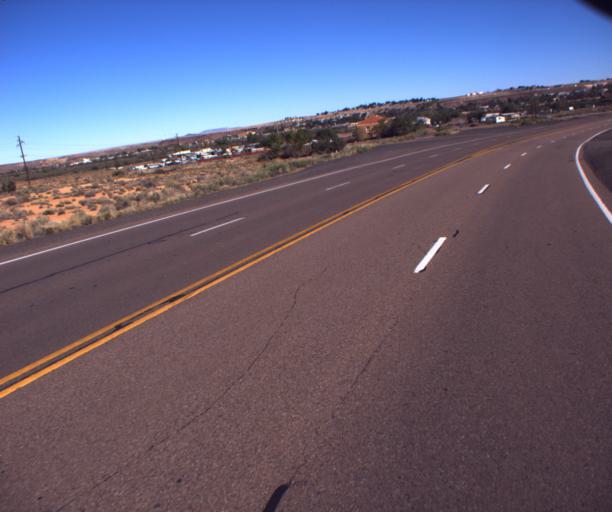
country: US
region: Arizona
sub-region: Navajo County
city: Holbrook
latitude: 34.8894
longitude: -110.1625
